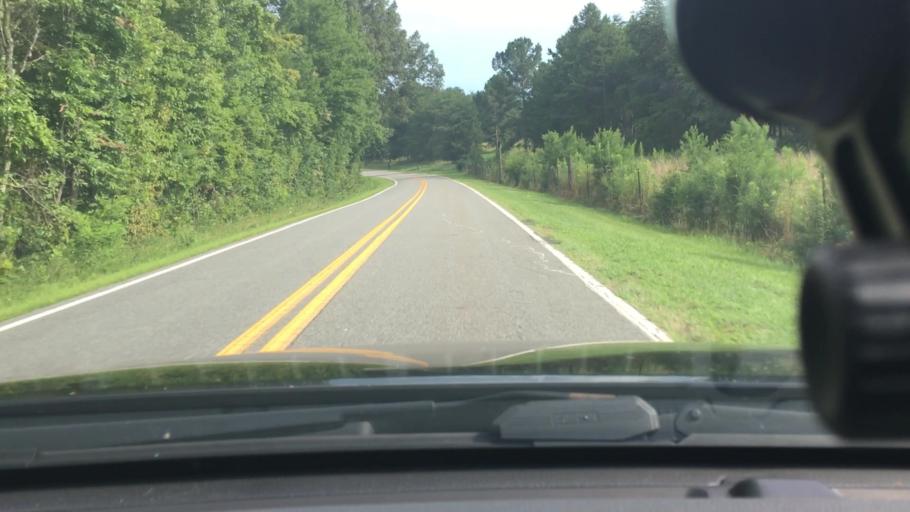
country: US
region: North Carolina
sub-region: Rutherford County
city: Rutherfordton
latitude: 35.4016
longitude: -81.9738
